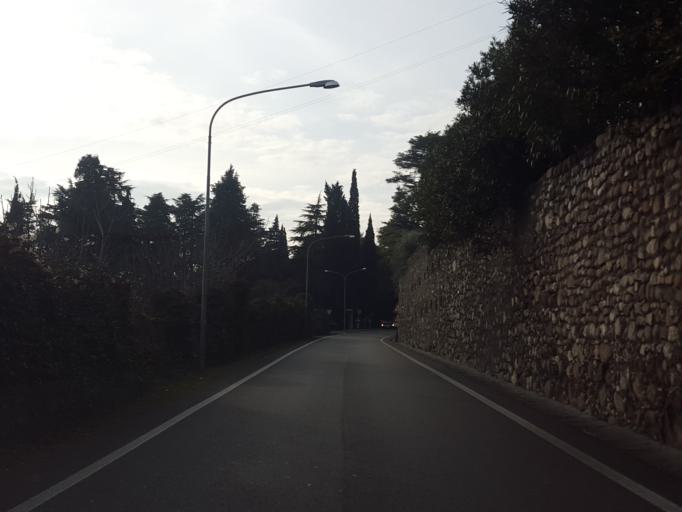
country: IT
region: Veneto
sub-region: Provincia di Verona
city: Costermano
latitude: 45.5869
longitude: 10.7460
